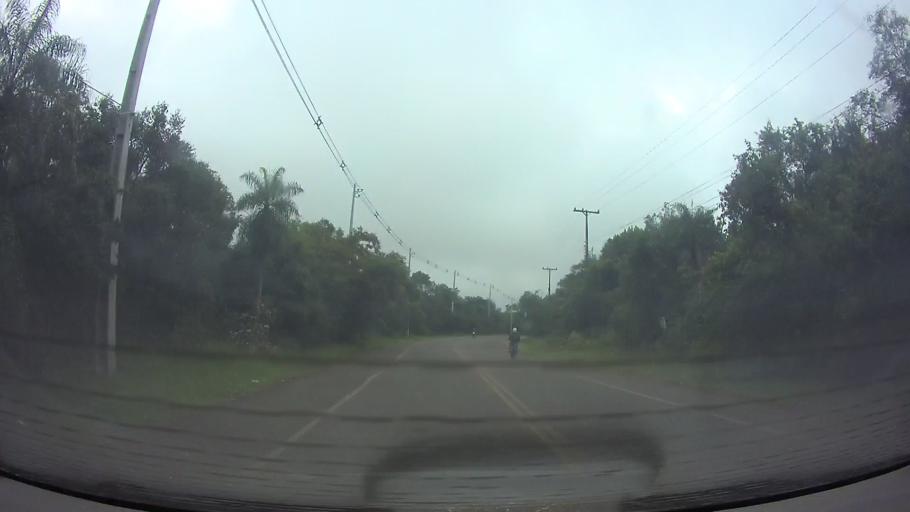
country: PY
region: Cordillera
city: Altos
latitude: -25.2826
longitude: -57.2620
